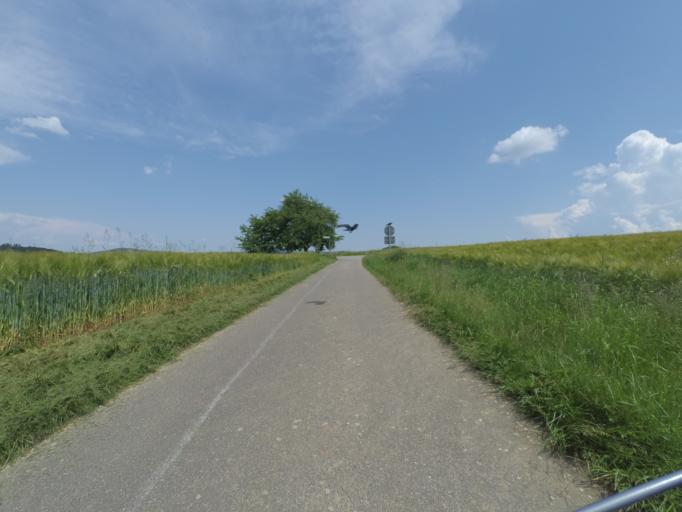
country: DE
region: Rheinland-Pfalz
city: Morshausen
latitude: 50.2041
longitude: 7.4349
